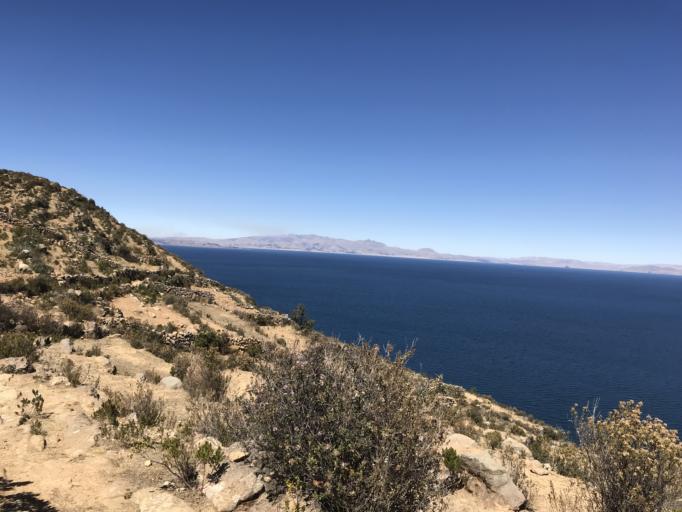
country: BO
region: La Paz
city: Yumani
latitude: -16.0392
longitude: -69.1491
